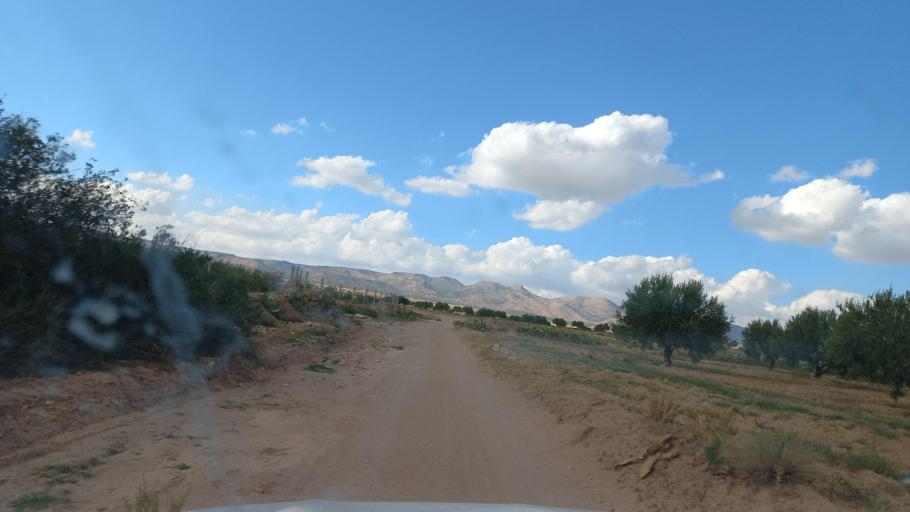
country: TN
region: Al Qasrayn
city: Sbiba
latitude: 35.3910
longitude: 9.0384
